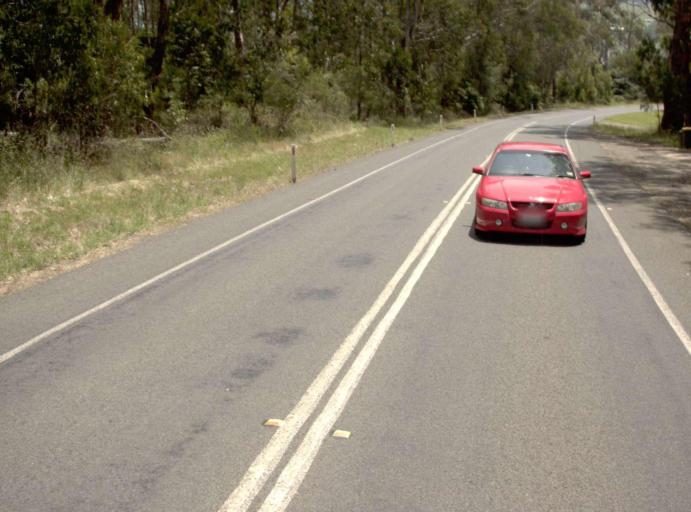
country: AU
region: Victoria
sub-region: Latrobe
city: Traralgon
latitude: -38.3787
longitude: 146.7552
